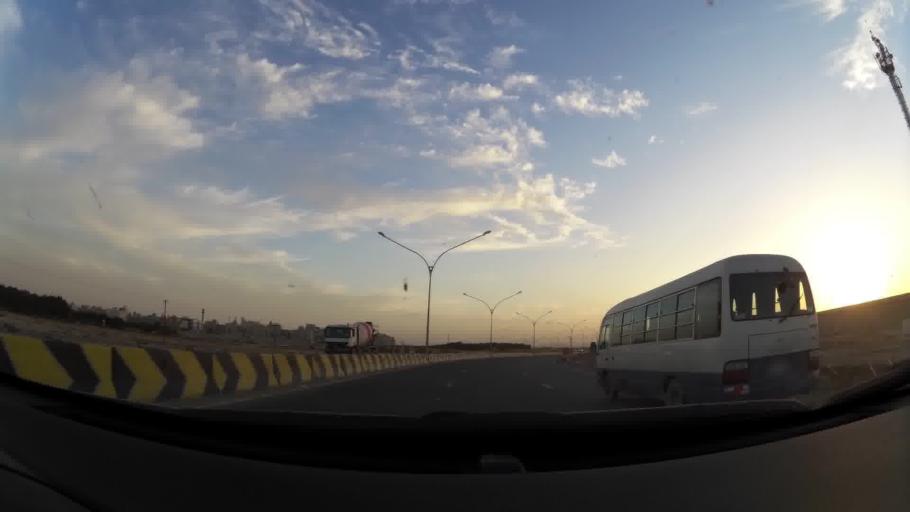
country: KW
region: Al Asimah
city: Ar Rabiyah
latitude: 29.3386
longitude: 47.8004
